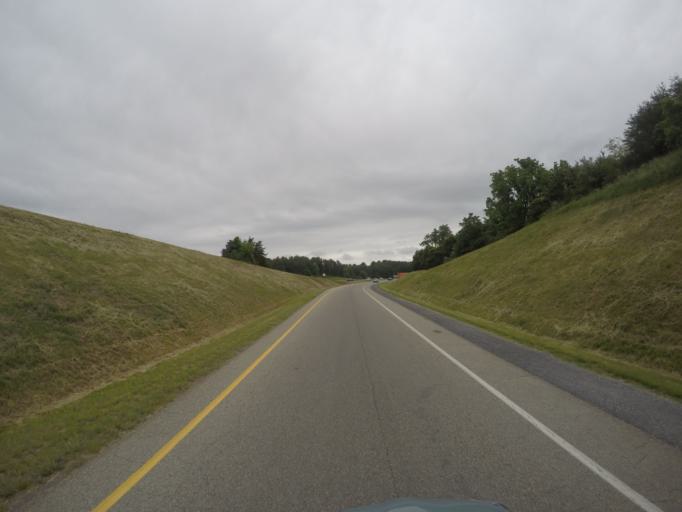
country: US
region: Virginia
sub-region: City of Staunton
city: Staunton
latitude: 38.1298
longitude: -79.0325
